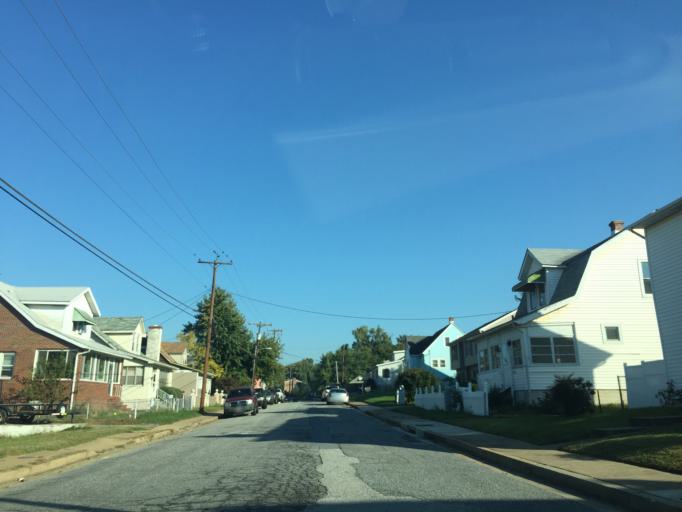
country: US
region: Maryland
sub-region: Baltimore County
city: Dundalk
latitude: 39.2836
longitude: -76.5270
